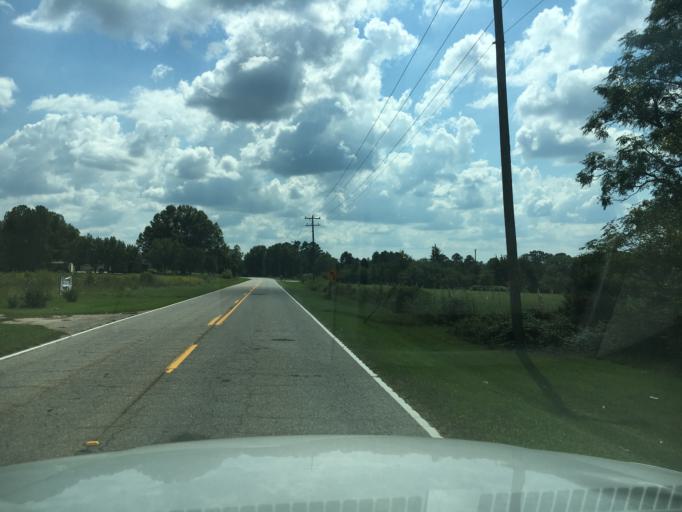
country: US
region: South Carolina
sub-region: Greenwood County
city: Greenwood
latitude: 34.0705
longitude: -82.1467
